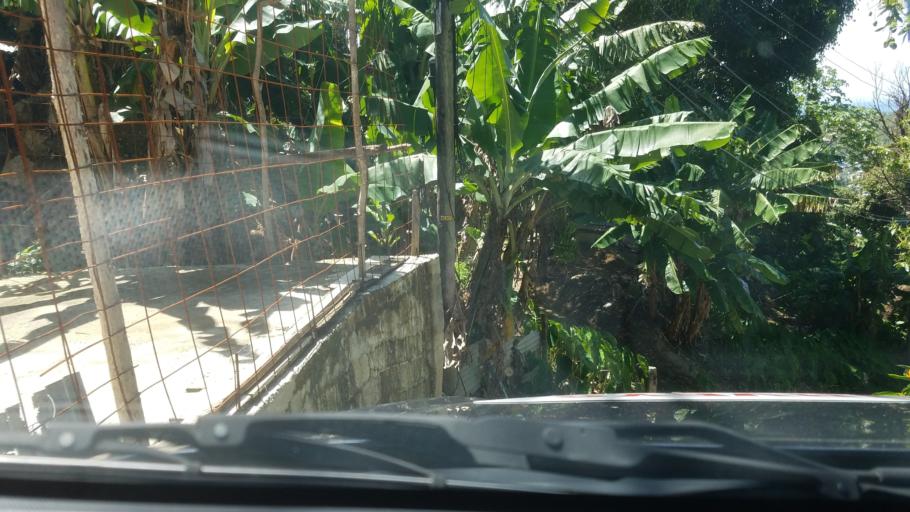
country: LC
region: Castries Quarter
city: Castries
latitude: 13.9985
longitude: -60.9869
